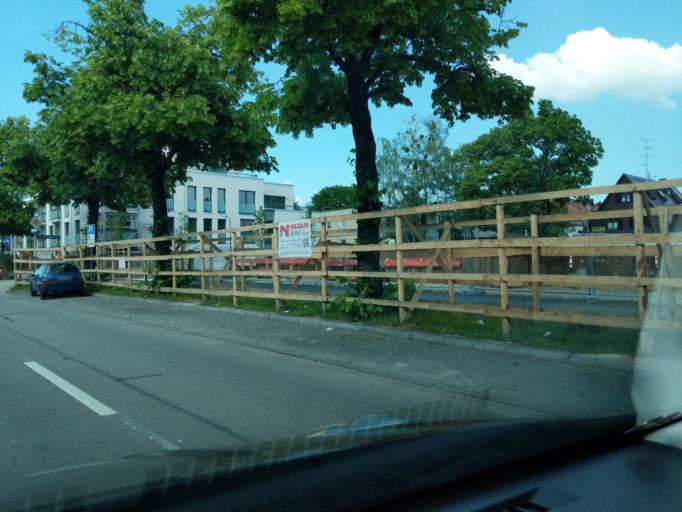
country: DE
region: Bavaria
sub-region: Upper Bavaria
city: Neuried
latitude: 48.1149
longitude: 11.5025
